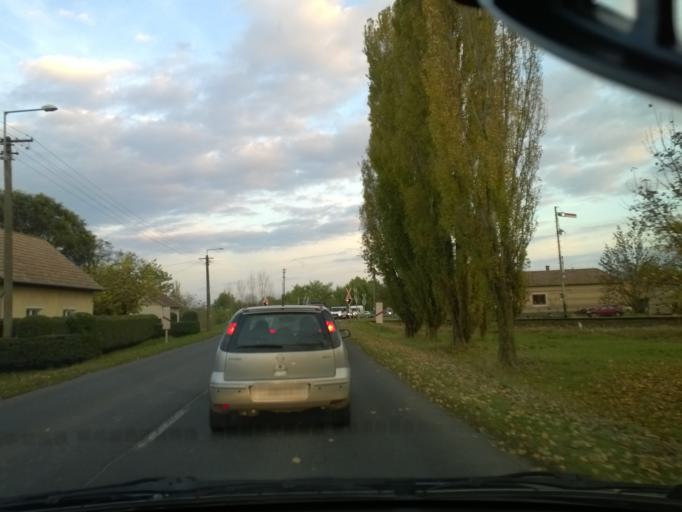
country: HU
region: Bacs-Kiskun
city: Palmonostora
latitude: 46.6850
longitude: 19.9545
